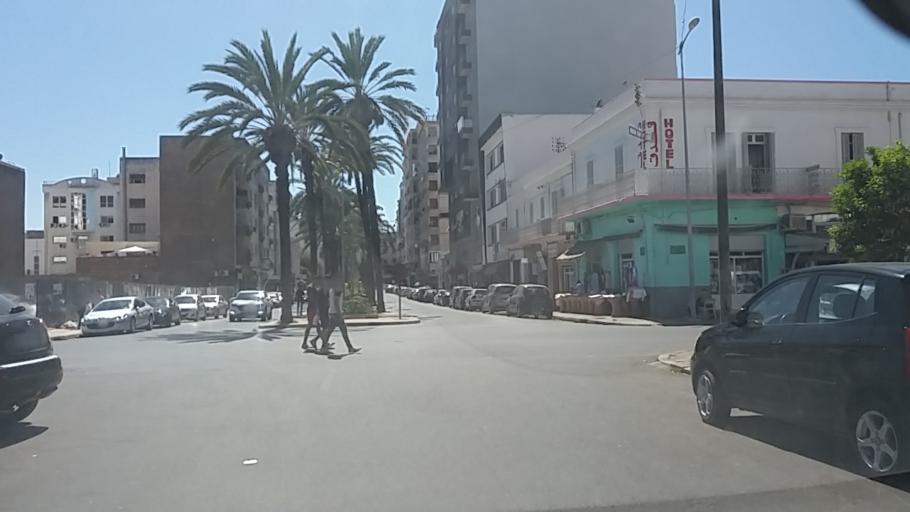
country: MA
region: Gharb-Chrarda-Beni Hssen
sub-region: Kenitra Province
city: Kenitra
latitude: 34.2617
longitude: -6.5831
